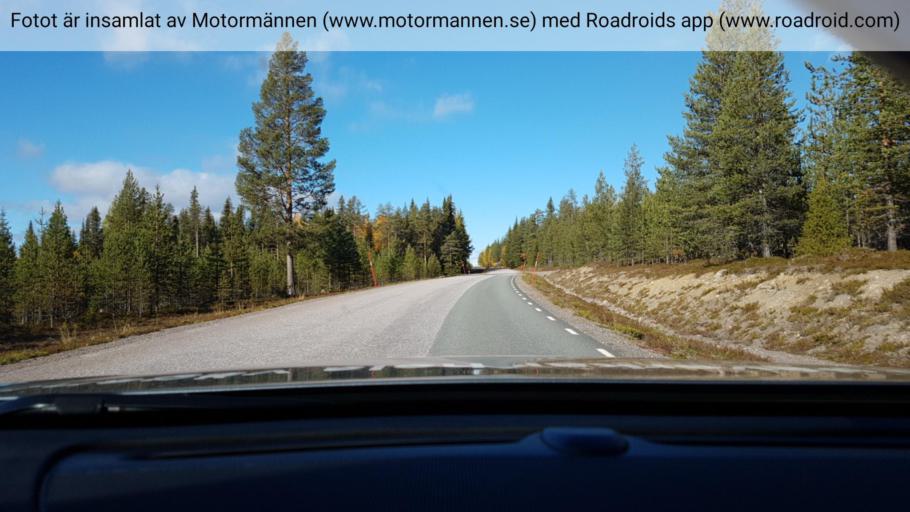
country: SE
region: Vaesterbotten
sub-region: Mala Kommun
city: Mala
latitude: 65.7653
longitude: 18.5504
